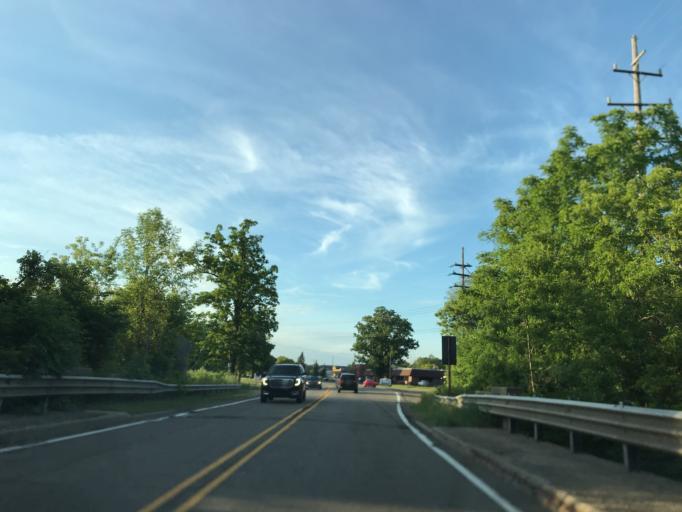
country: US
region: Michigan
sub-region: Wayne County
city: Northville
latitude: 42.4423
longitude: -83.4741
